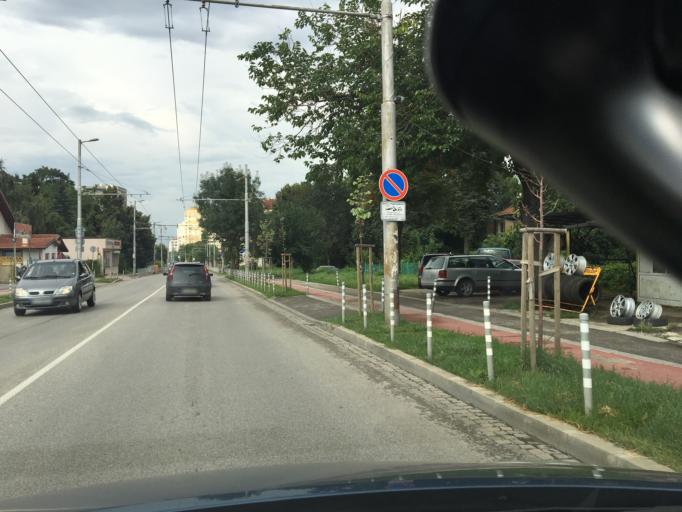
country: BG
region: Sofia-Capital
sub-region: Stolichna Obshtina
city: Sofia
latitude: 42.6655
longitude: 23.2754
